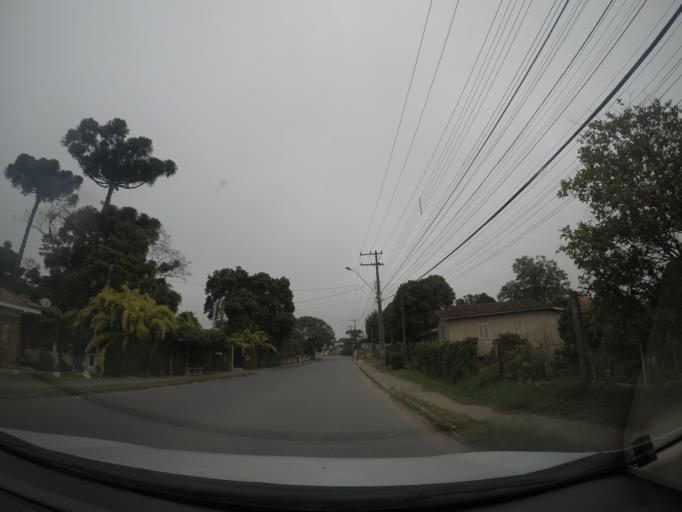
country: BR
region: Parana
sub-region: Almirante Tamandare
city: Almirante Tamandare
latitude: -25.3450
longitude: -49.2567
